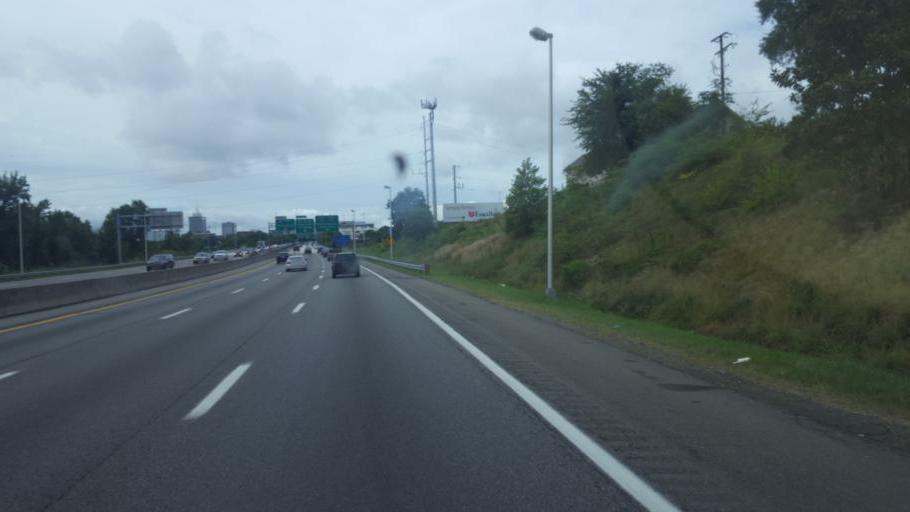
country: US
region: Virginia
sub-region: Henrico County
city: East Highland Park
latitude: 37.5561
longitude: -77.4244
